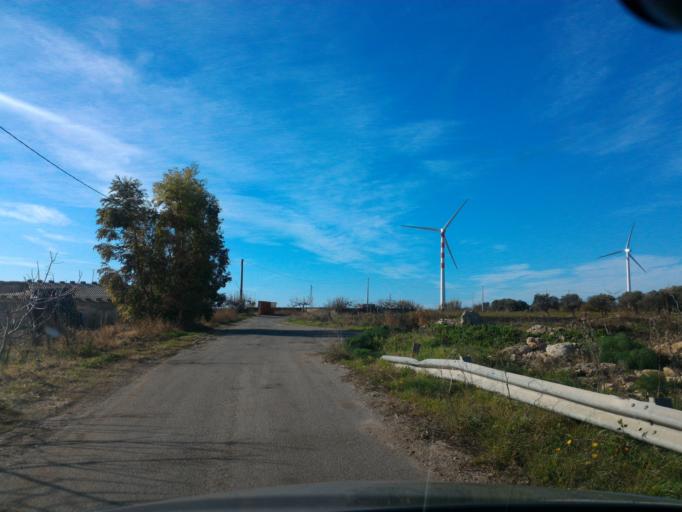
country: IT
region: Calabria
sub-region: Provincia di Crotone
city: Isola di Capo Rizzuto
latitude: 38.9453
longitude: 17.0558
